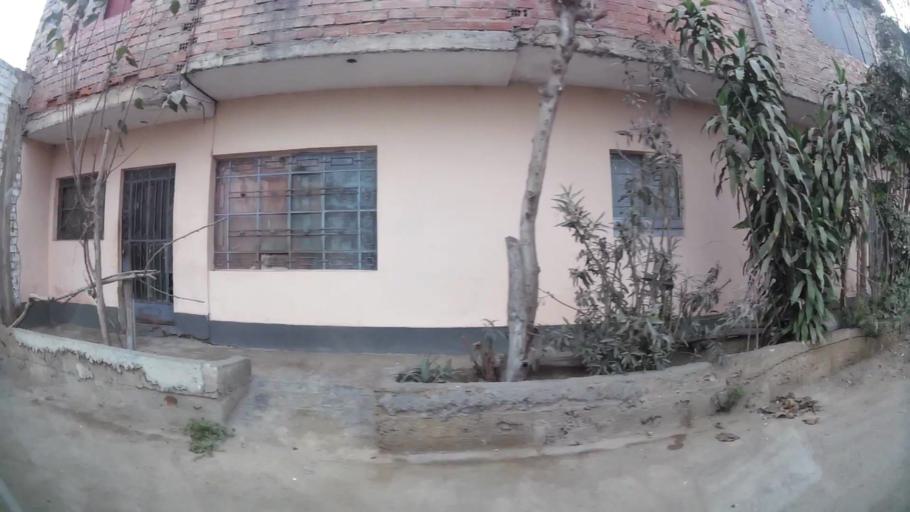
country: PE
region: Lima
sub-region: Lima
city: Surco
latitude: -12.1563
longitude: -76.9619
